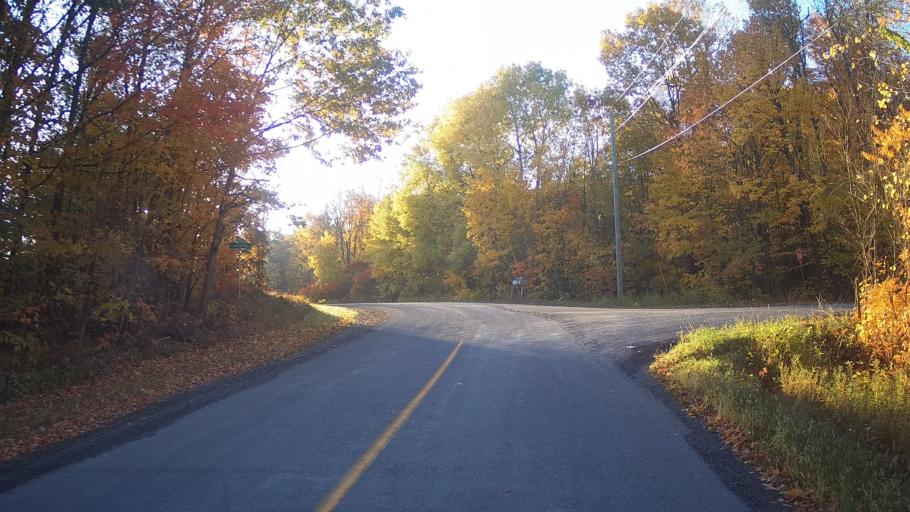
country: CA
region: Ontario
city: Arnprior
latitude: 45.3455
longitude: -76.3364
